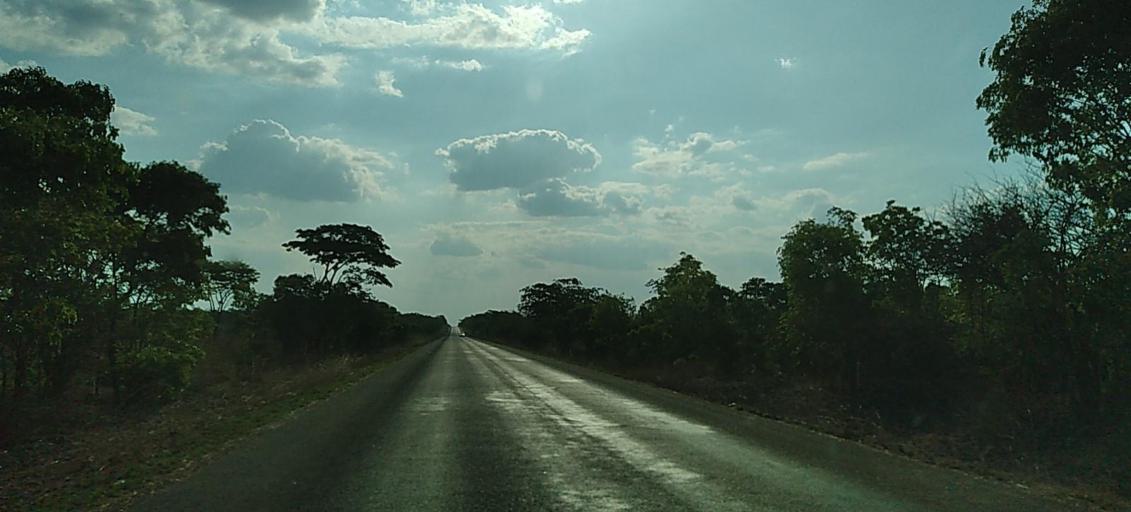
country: ZM
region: Copperbelt
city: Mpongwe
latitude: -13.3913
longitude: 28.3699
